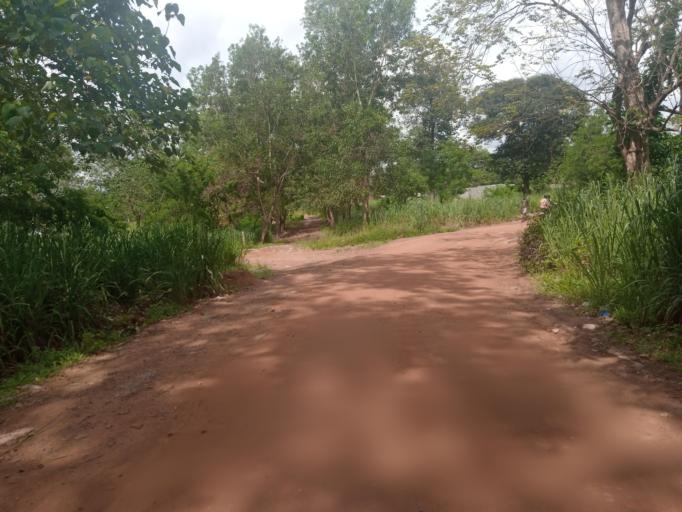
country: SL
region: Southern Province
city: Bo
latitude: 7.9680
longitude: -11.7485
